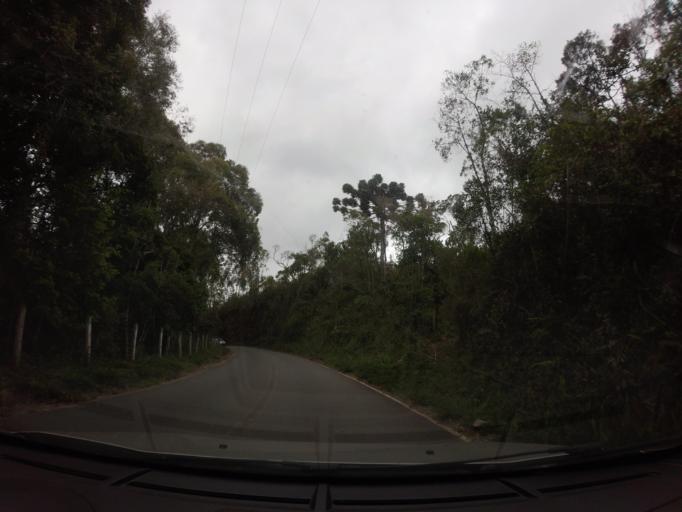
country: BR
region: Sao Paulo
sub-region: Campos Do Jordao
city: Campos do Jordao
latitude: -22.6609
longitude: -45.6037
